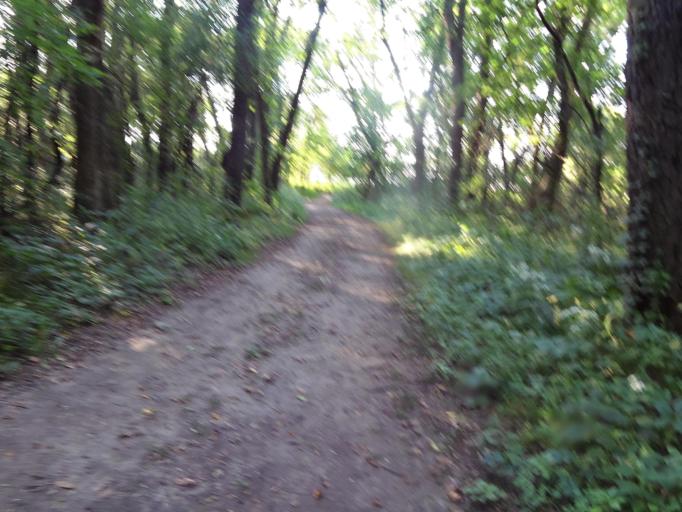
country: US
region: Minnesota
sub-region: Washington County
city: Afton
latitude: 44.8411
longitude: -92.7766
